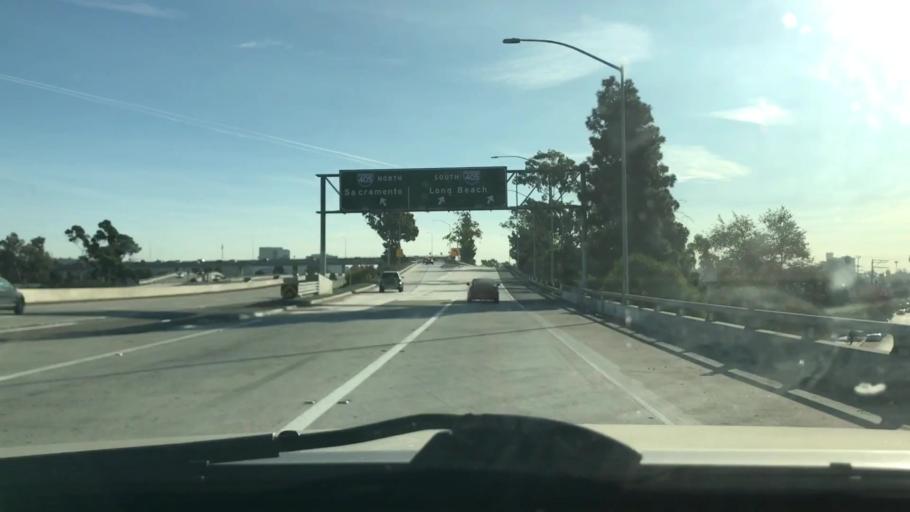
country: US
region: California
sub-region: Los Angeles County
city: Ladera Heights
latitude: 33.9879
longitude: -118.4036
